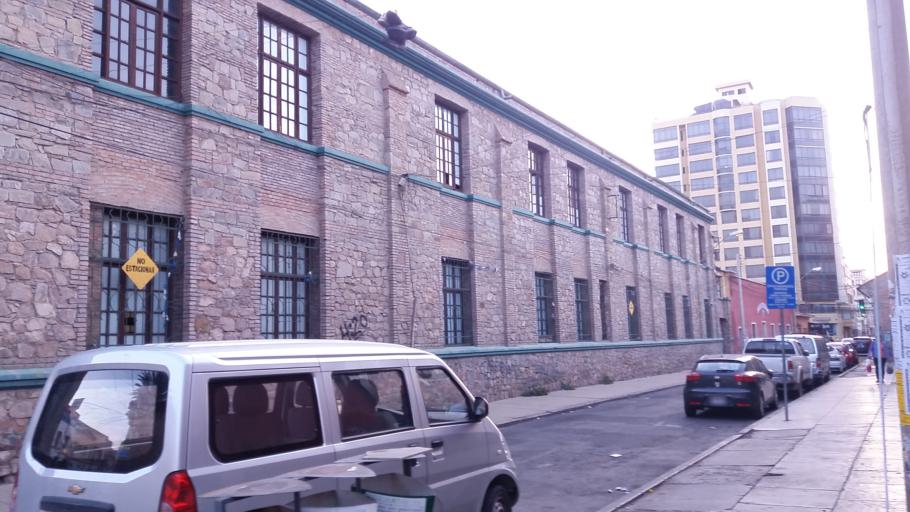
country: BO
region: Cochabamba
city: Cochabamba
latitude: -17.3902
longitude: -66.1583
